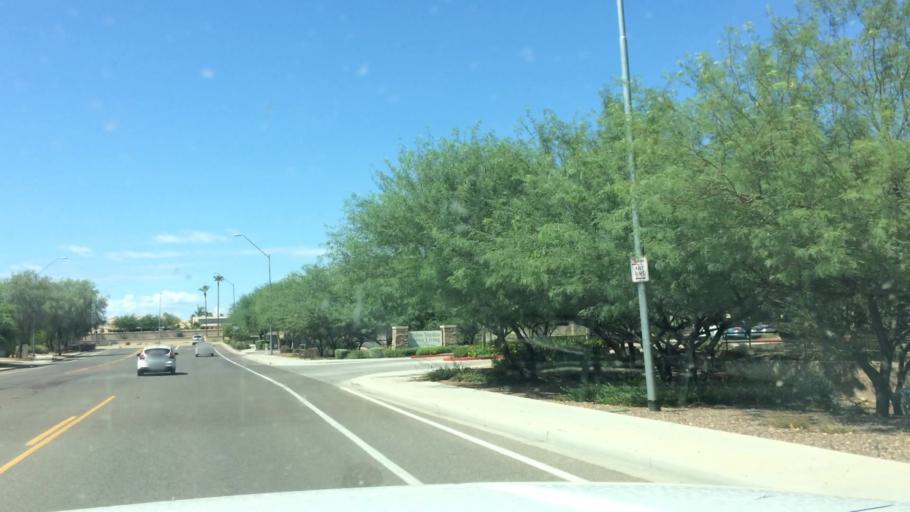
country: US
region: Arizona
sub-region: Maricopa County
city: Sun City
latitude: 33.6510
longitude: -112.2463
